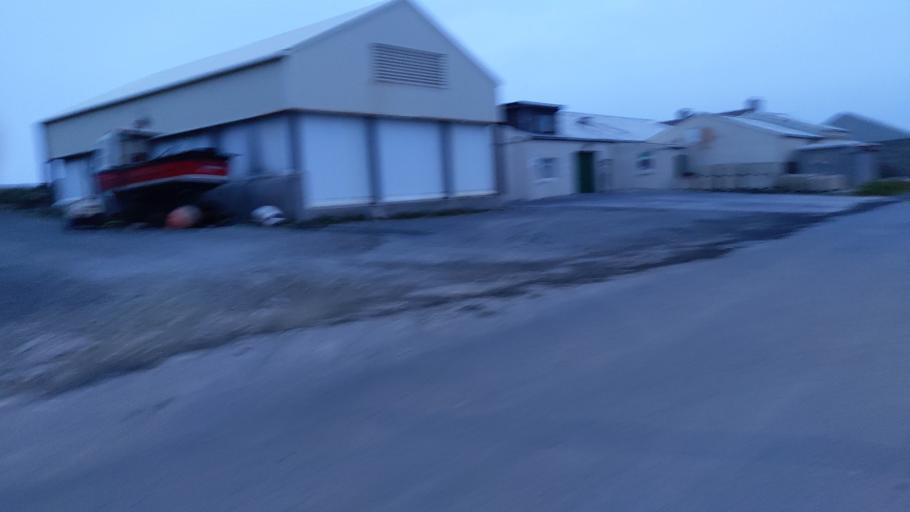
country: GB
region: Scotland
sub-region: Orkney Islands
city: Kirkwall
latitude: 59.3243
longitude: -2.9752
